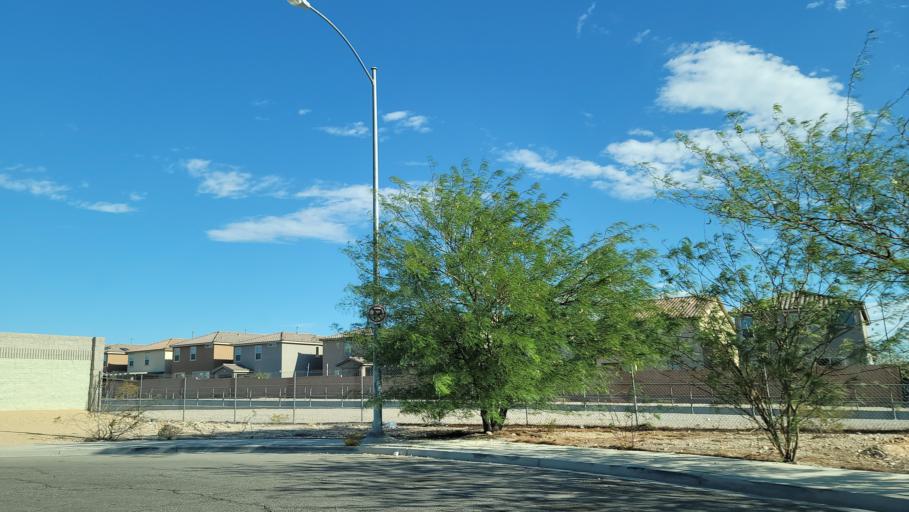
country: US
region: Nevada
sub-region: Clark County
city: Spring Valley
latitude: 36.0869
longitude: -115.2815
